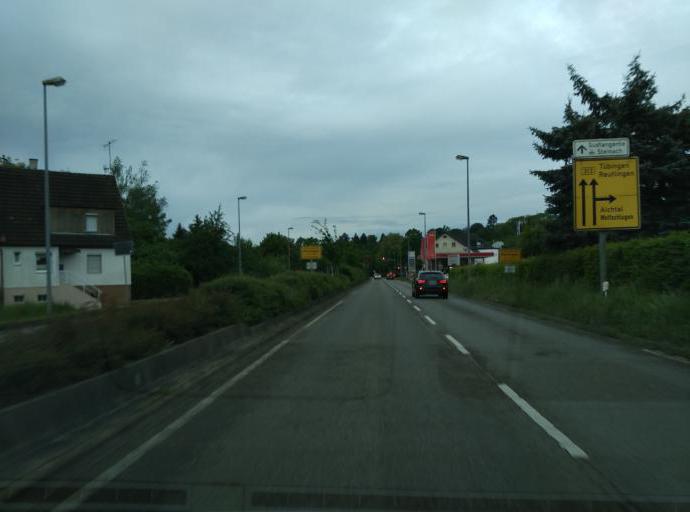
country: DE
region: Baden-Wuerttemberg
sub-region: Regierungsbezirk Stuttgart
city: Nurtingen
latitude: 48.6350
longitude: 9.3290
